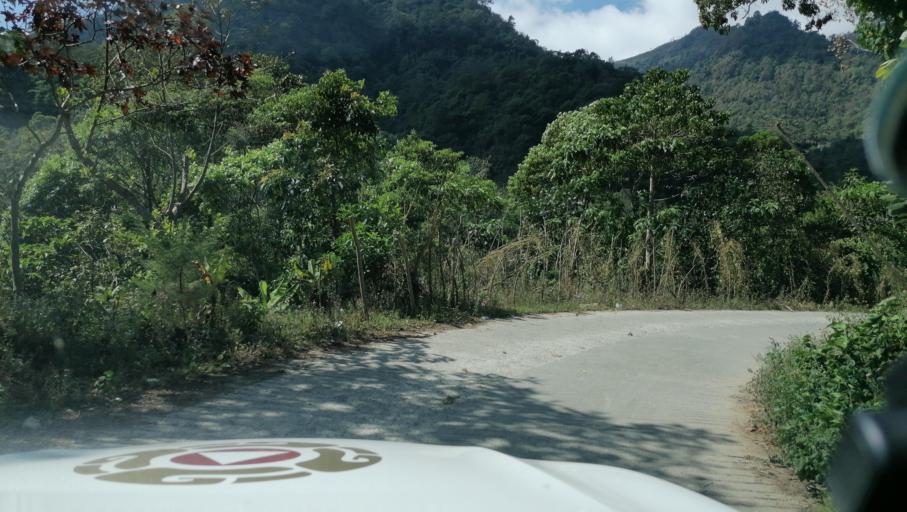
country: GT
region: San Marcos
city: Tacana
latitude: 15.2026
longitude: -92.2007
